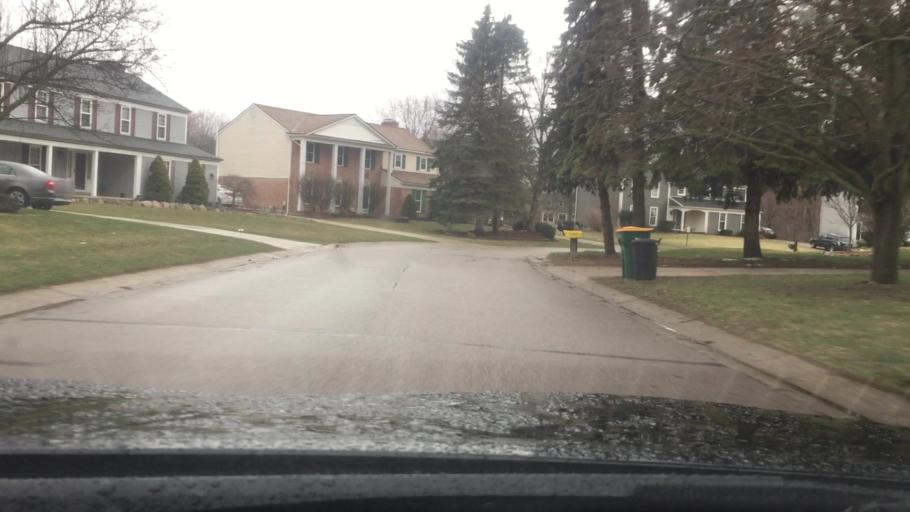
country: US
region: Michigan
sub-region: Oakland County
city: Farmington Hills
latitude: 42.5055
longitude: -83.4024
